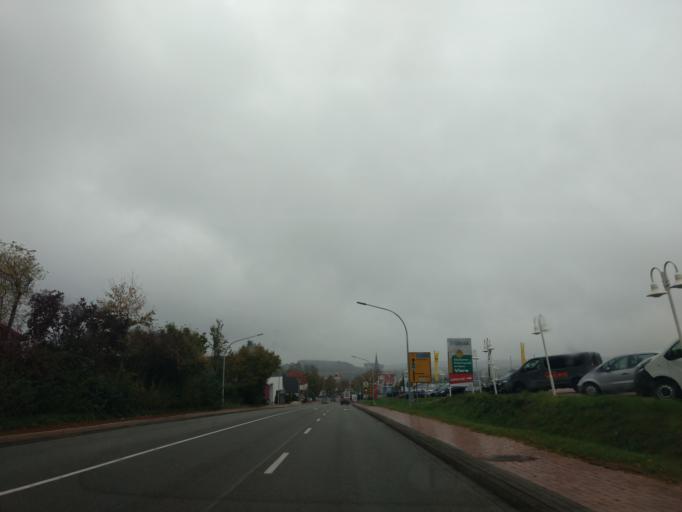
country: DE
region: Lower Saxony
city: Georgsmarienhutte
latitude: 52.1977
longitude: 8.0686
